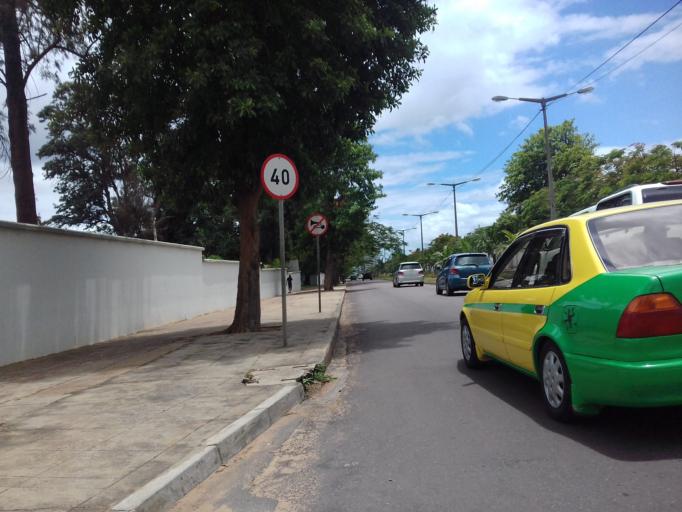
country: MZ
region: Maputo City
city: Maputo
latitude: -25.9665
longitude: 32.5985
